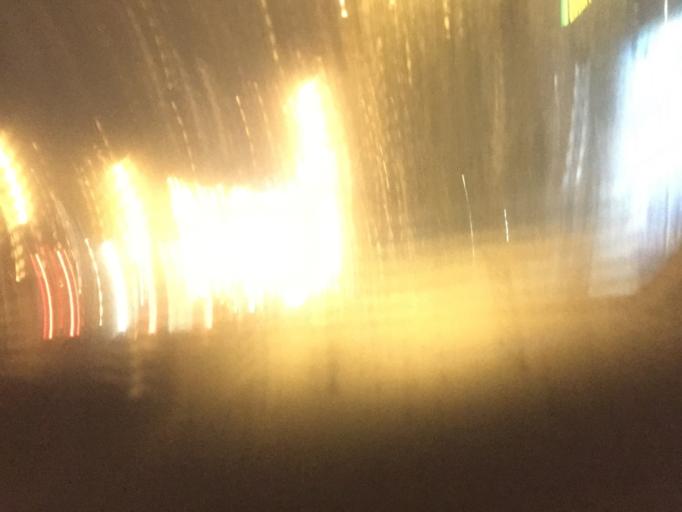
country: KZ
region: Astana Qalasy
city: Astana
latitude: 51.1644
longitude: 71.4278
